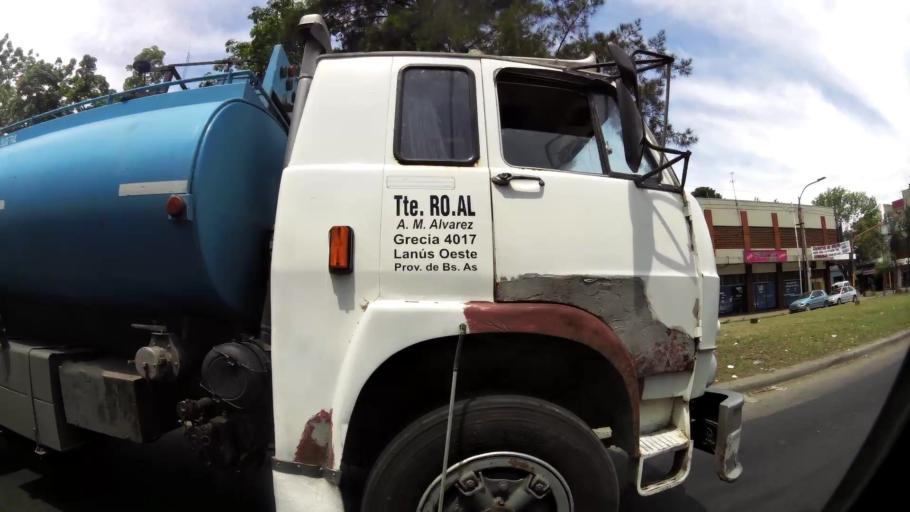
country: AR
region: Buenos Aires
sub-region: Partido de Lanus
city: Lanus
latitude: -34.6770
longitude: -58.4007
